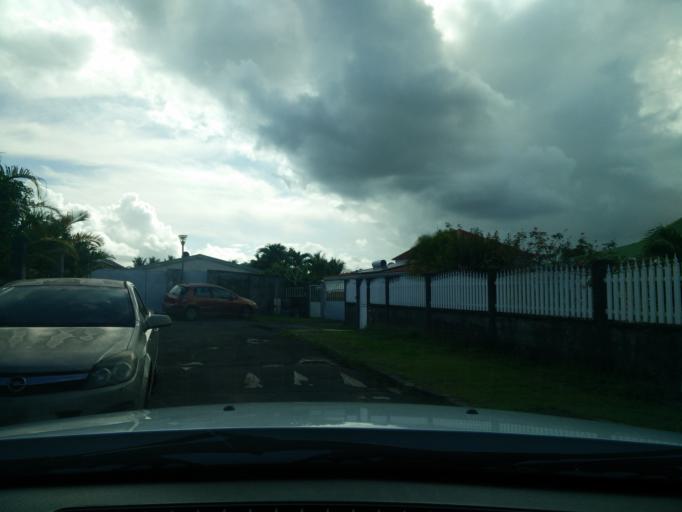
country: GP
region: Guadeloupe
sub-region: Guadeloupe
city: Baie-Mahault
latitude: 16.2587
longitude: -61.5814
